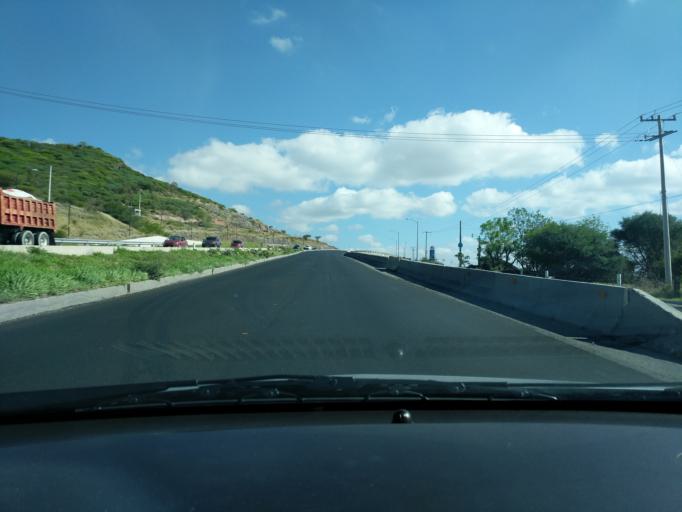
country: MX
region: Guanajuato
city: El Castillo
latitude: 20.6026
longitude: -100.4912
